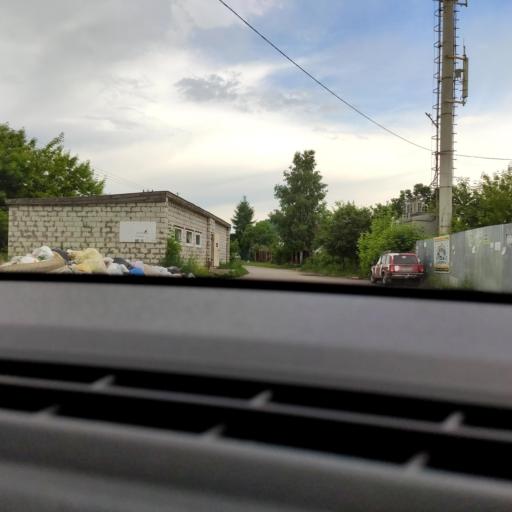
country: RU
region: Samara
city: Podstepki
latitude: 53.5137
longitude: 49.0705
